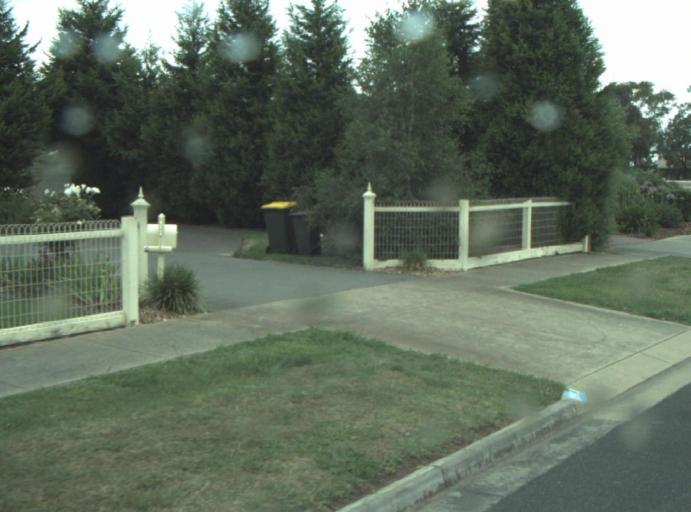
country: AU
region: Victoria
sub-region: Greater Geelong
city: Breakwater
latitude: -38.1957
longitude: 144.3915
